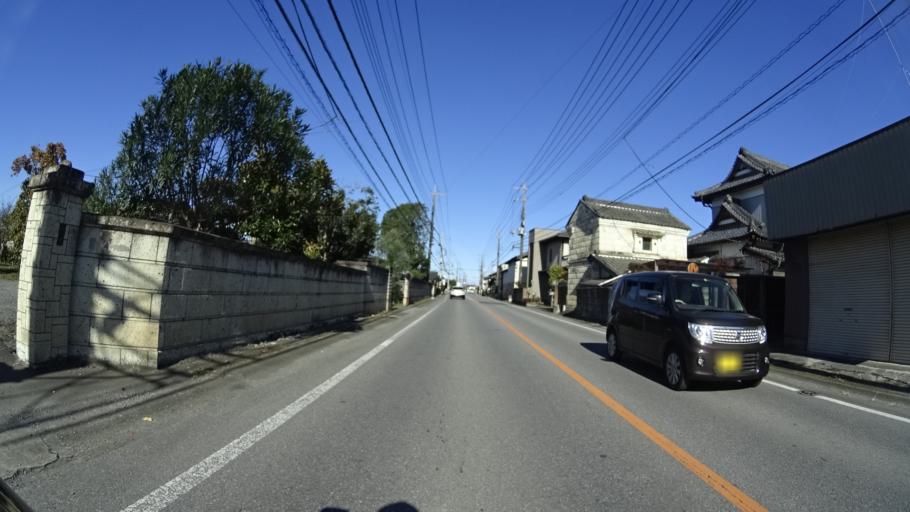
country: JP
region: Tochigi
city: Tochigi
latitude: 36.4135
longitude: 139.7474
